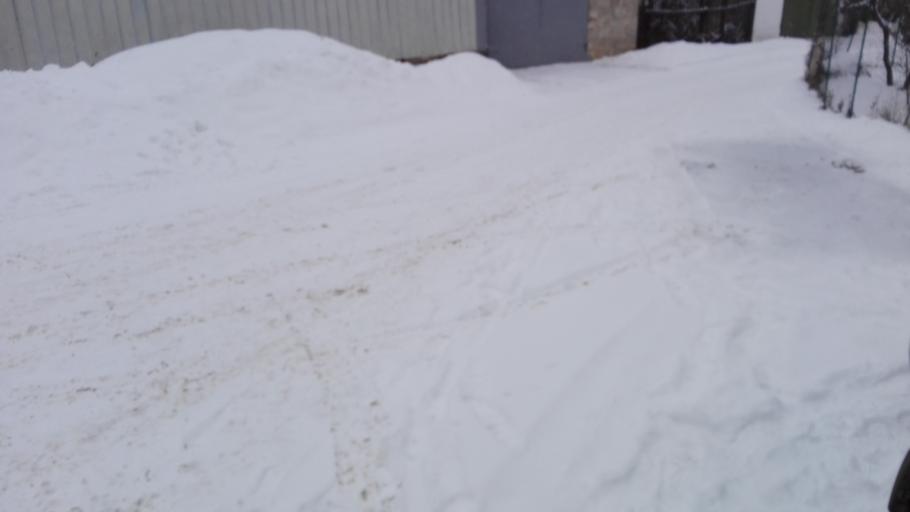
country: RU
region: Tula
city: Kosaya Gora
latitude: 54.1180
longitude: 37.5347
